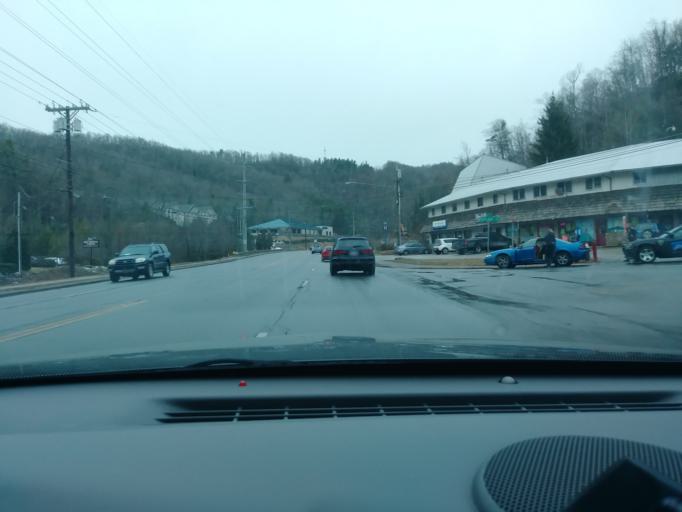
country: US
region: North Carolina
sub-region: Watauga County
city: Boone
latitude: 36.2026
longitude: -81.6772
